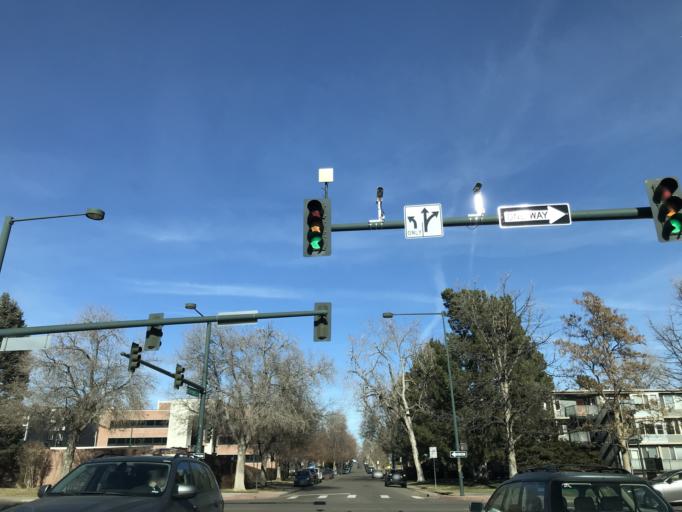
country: US
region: Colorado
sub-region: Arapahoe County
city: Glendale
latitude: 39.7335
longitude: -104.9349
